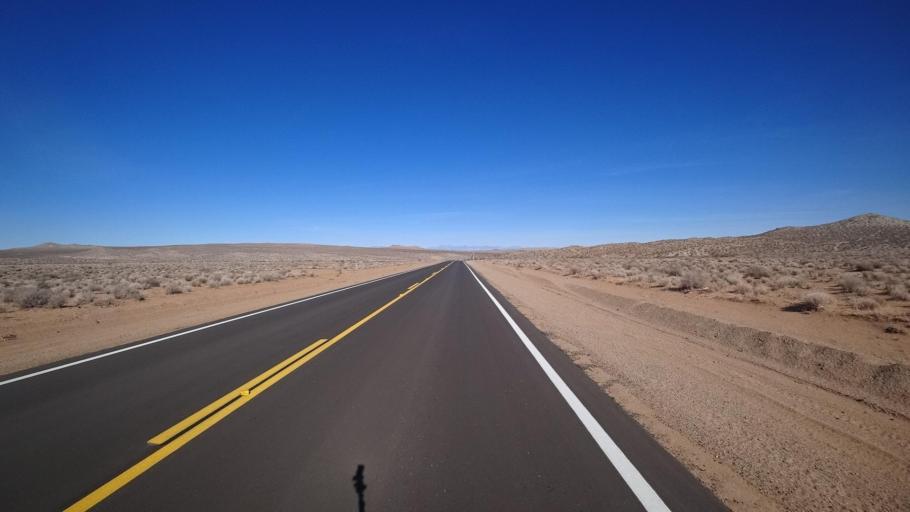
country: US
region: California
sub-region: Kern County
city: Ridgecrest
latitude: 35.4952
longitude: -117.6272
